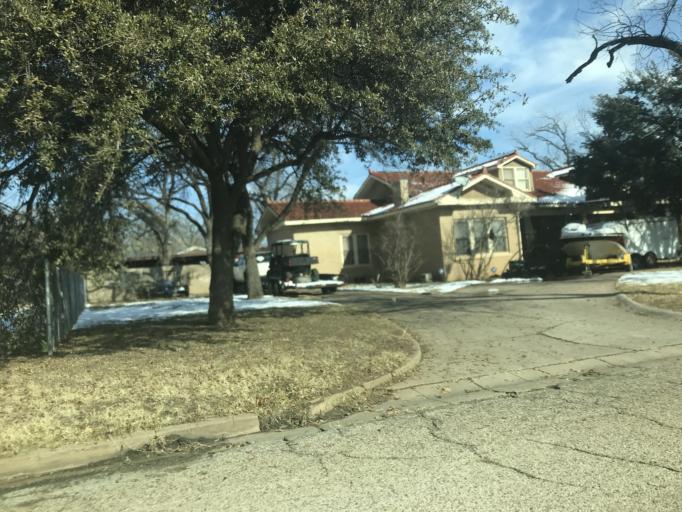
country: US
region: Texas
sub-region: Taylor County
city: Abilene
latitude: 32.4656
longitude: -99.7389
